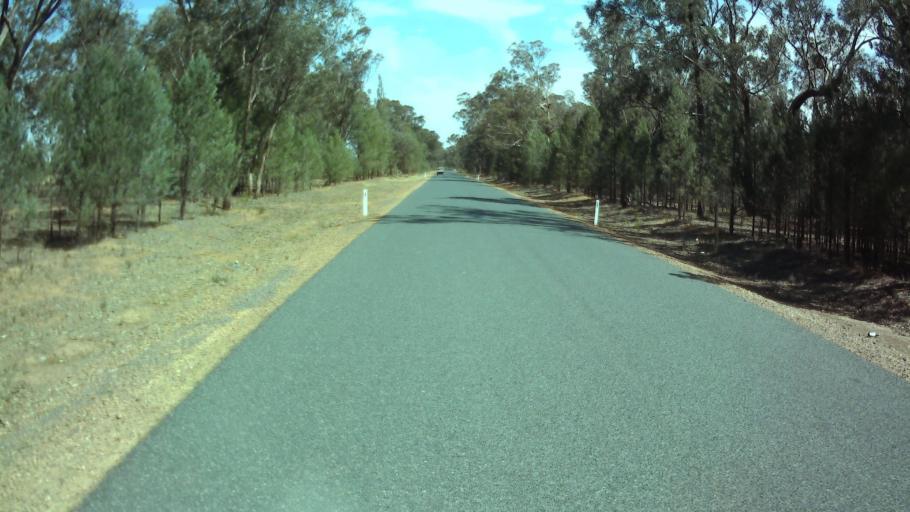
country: AU
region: New South Wales
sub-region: Weddin
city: Grenfell
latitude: -34.0328
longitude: 148.1338
